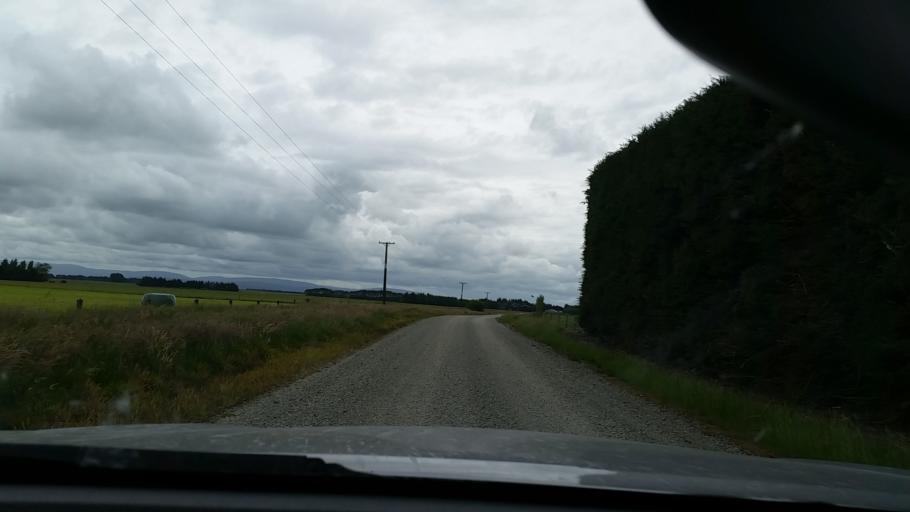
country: NZ
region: Southland
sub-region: Southland District
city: Winton
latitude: -46.1934
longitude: 168.2436
